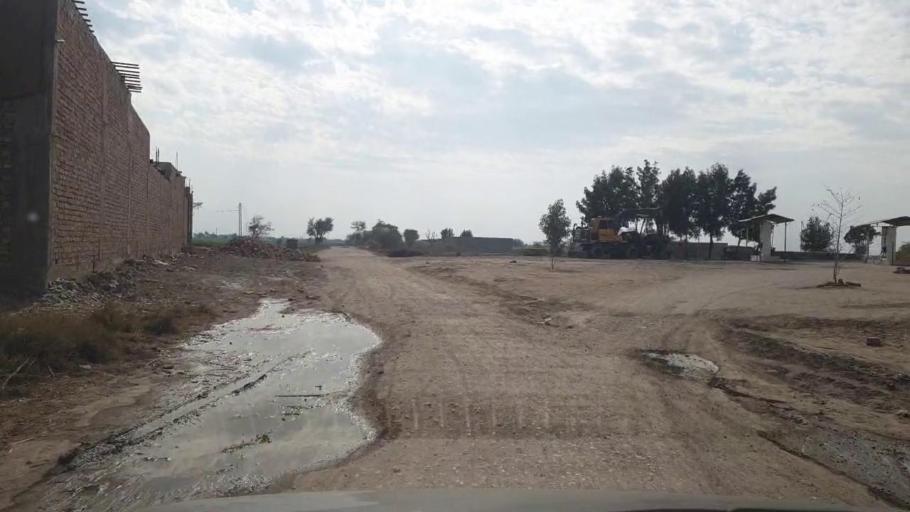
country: PK
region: Sindh
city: Sakrand
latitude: 26.0122
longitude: 68.4082
